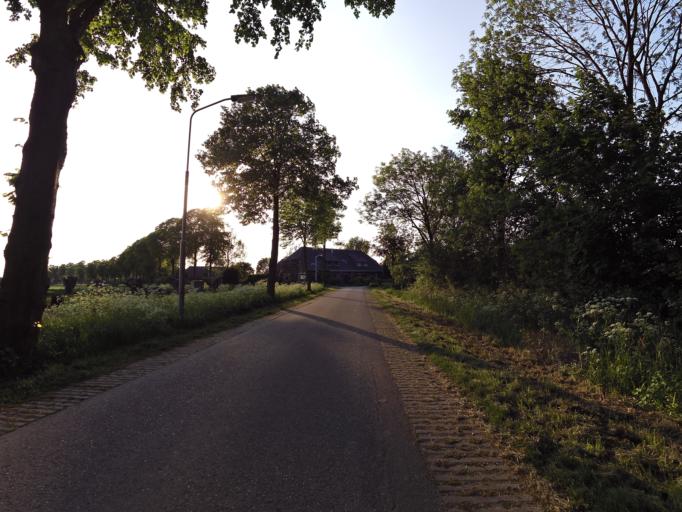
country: NL
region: Gelderland
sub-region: Gemeente Montferland
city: s-Heerenberg
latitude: 51.8522
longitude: 6.3109
